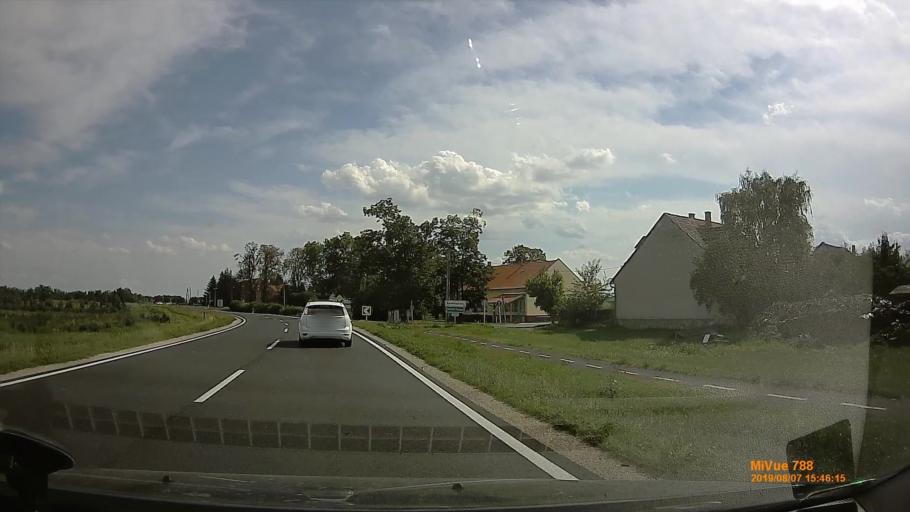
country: HU
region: Vas
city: Szombathely
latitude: 47.1870
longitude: 16.6203
